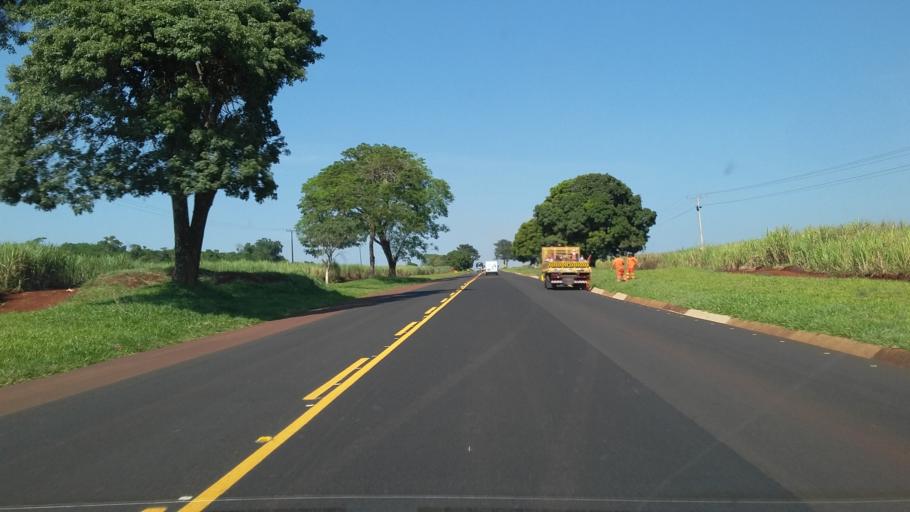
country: BR
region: Parana
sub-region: Bandeirantes
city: Bandeirantes
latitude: -23.1282
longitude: -50.4629
